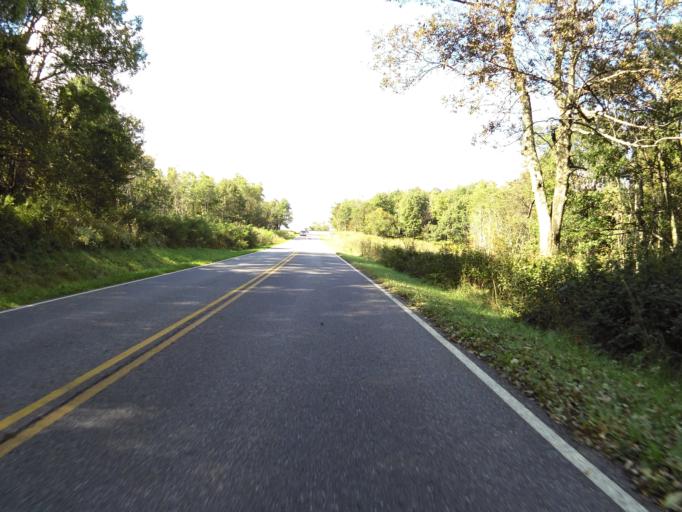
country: US
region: Virginia
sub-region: Page County
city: Stanley
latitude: 38.5444
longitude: -78.4141
